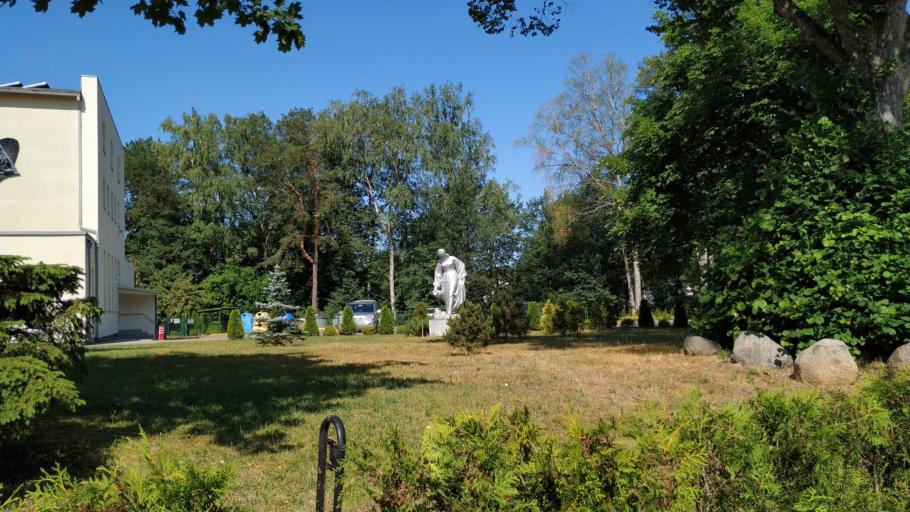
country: LT
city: Nemencine
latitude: 54.7938
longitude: 25.3976
